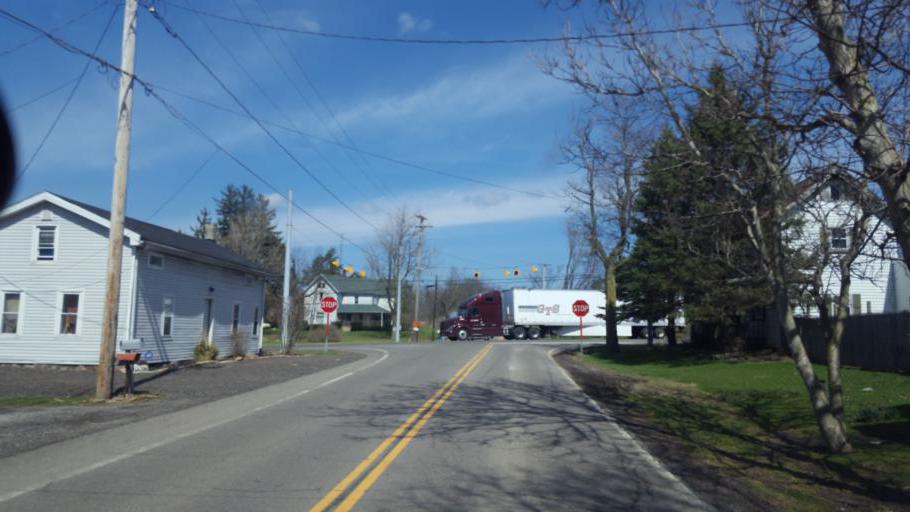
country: US
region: Ohio
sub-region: Ashland County
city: Ashland
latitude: 40.8876
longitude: -82.4262
